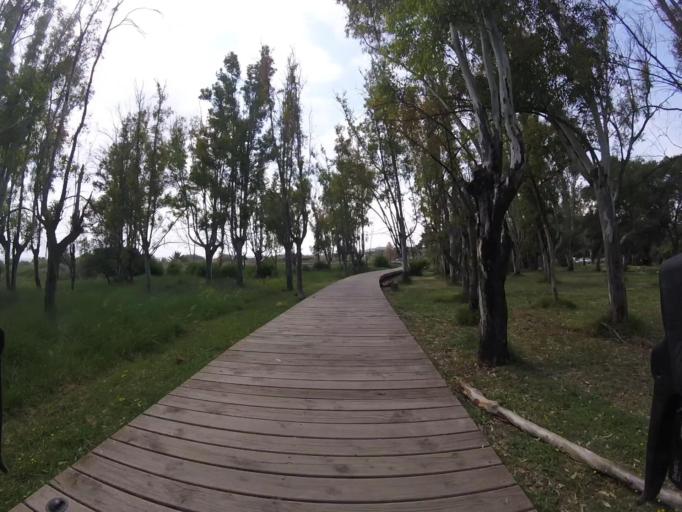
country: ES
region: Valencia
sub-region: Provincia de Castello
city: Orpesa/Oropesa del Mar
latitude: 40.1308
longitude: 0.1635
